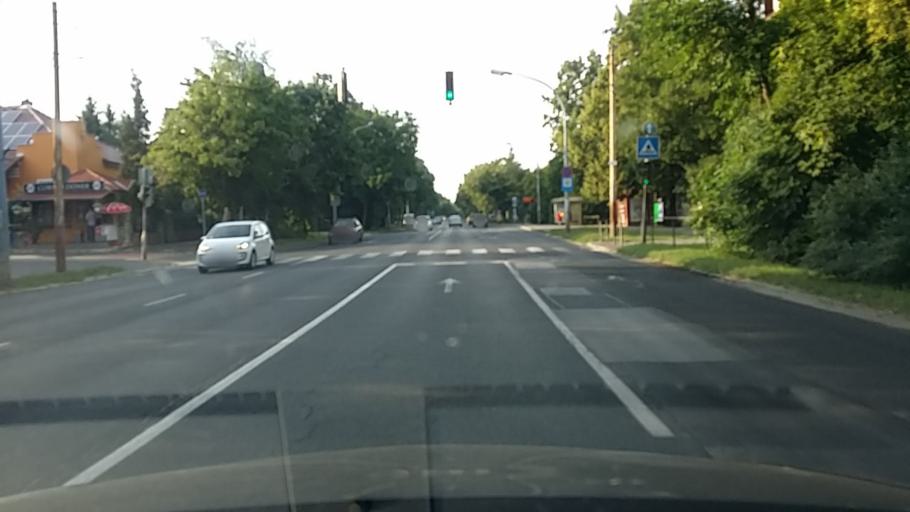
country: HU
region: Borsod-Abauj-Zemplen
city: Miskolc
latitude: 48.0853
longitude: 20.7855
